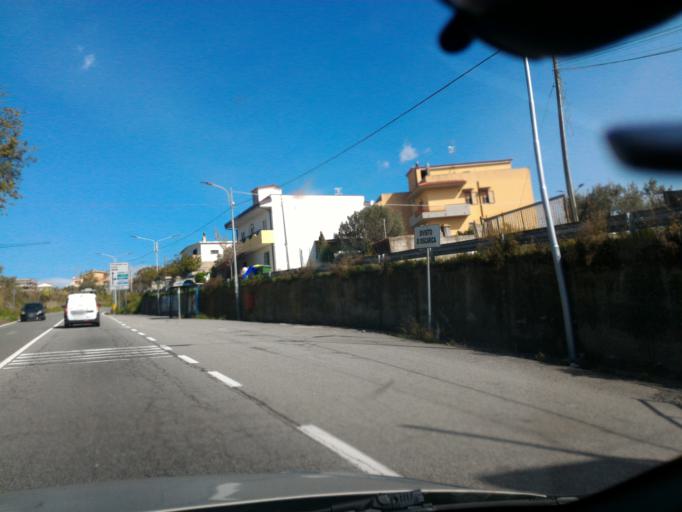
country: IT
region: Calabria
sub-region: Provincia di Catanzaro
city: Siano
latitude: 38.9096
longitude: 16.6016
